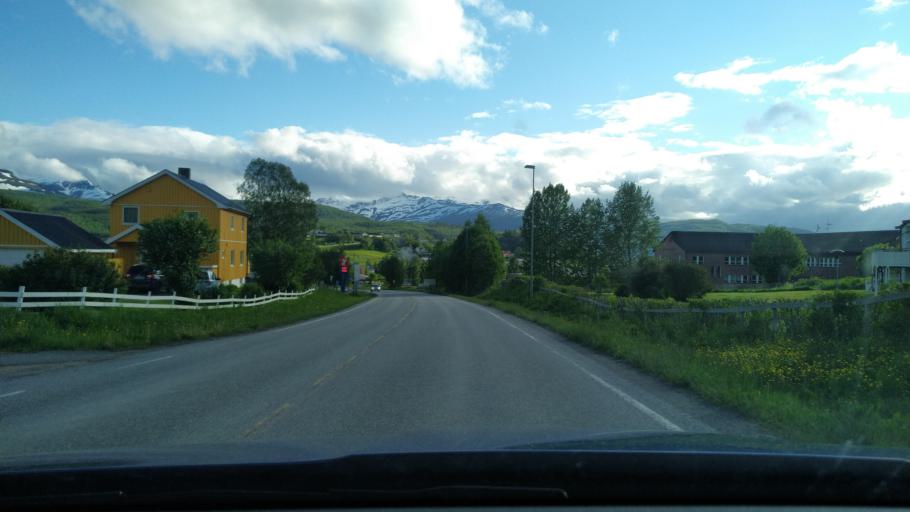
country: NO
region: Troms
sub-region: Sorreisa
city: Sorreisa
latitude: 69.1474
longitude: 18.1600
